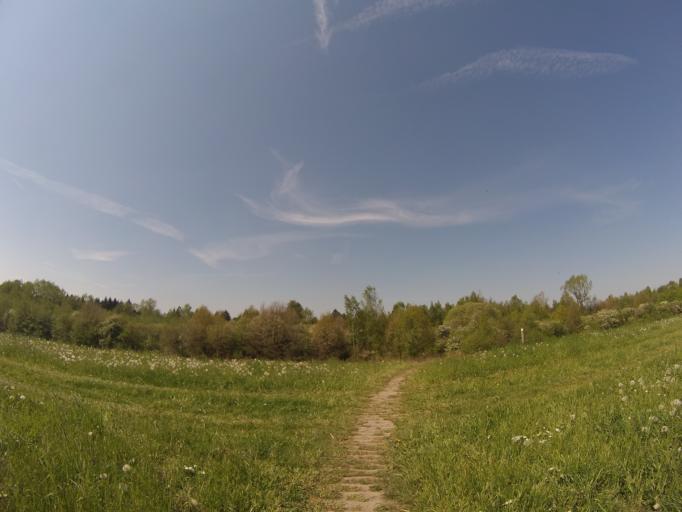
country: NL
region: Flevoland
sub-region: Gemeente Zeewolde
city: Zeewolde
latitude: 52.2995
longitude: 5.5393
